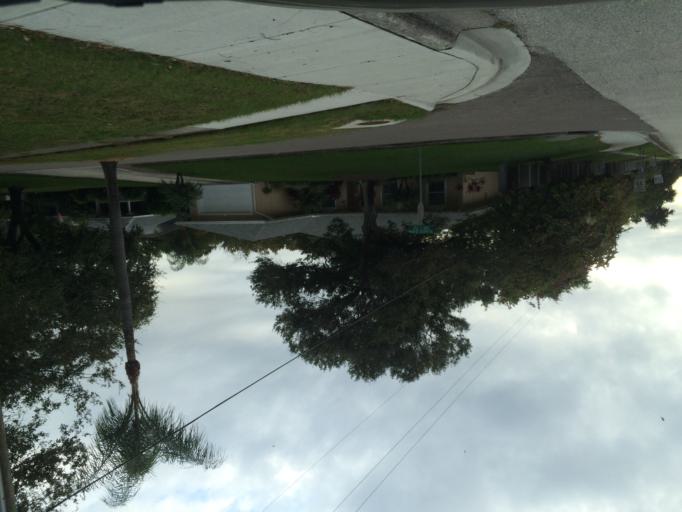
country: US
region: Florida
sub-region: Pinellas County
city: Gandy
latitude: 27.8505
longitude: -82.6254
